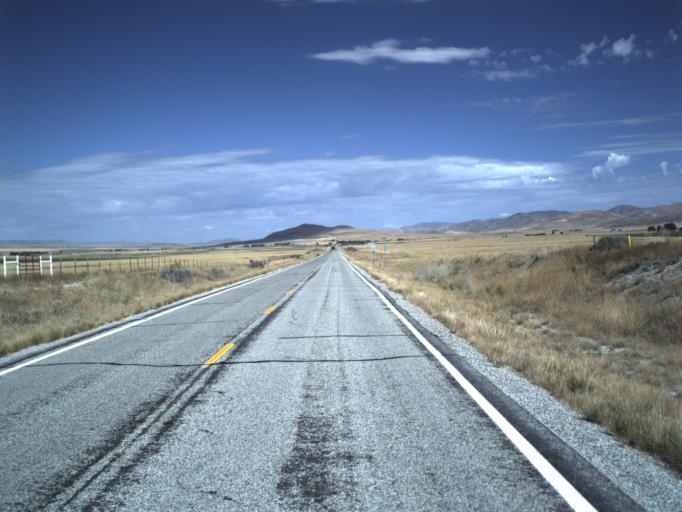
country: US
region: Utah
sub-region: Box Elder County
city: Tremonton
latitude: 41.7252
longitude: -112.4337
